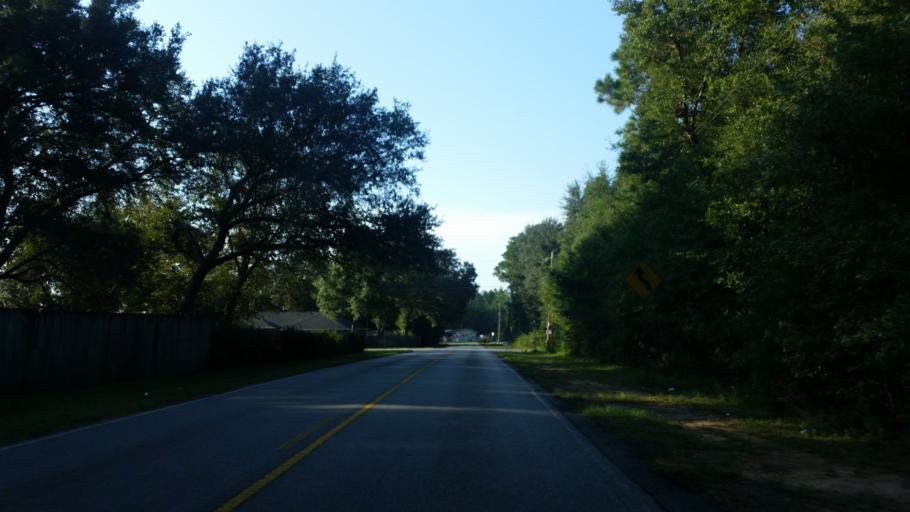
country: US
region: Florida
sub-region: Santa Rosa County
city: Milton
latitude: 30.6384
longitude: -87.0660
